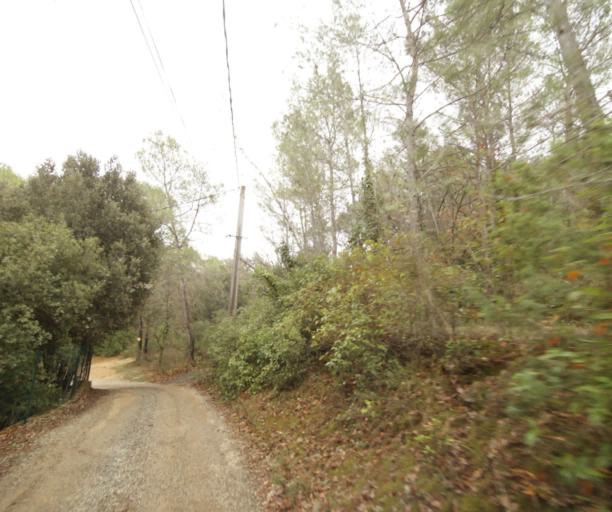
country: FR
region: Provence-Alpes-Cote d'Azur
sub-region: Departement du Var
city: Trans-en-Provence
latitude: 43.5144
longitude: 6.4854
